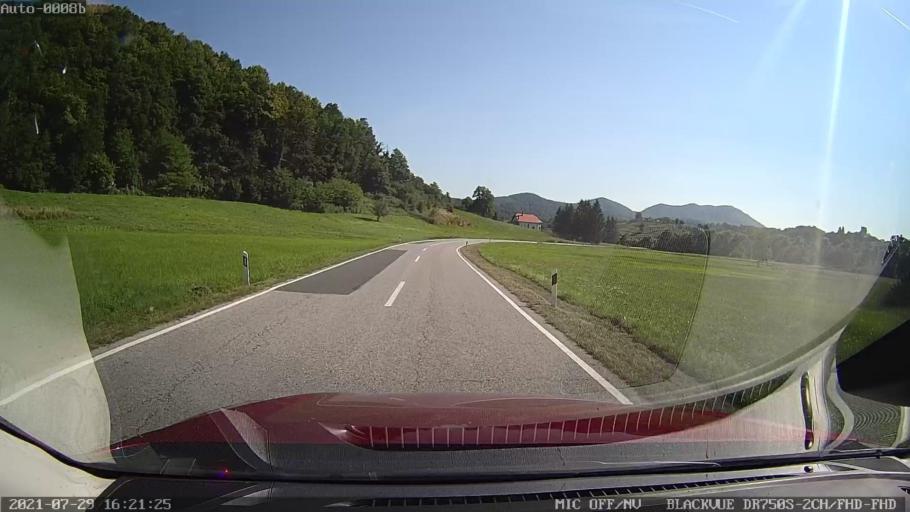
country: HR
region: Varazdinska
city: Lepoglava
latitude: 46.2352
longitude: 15.9678
